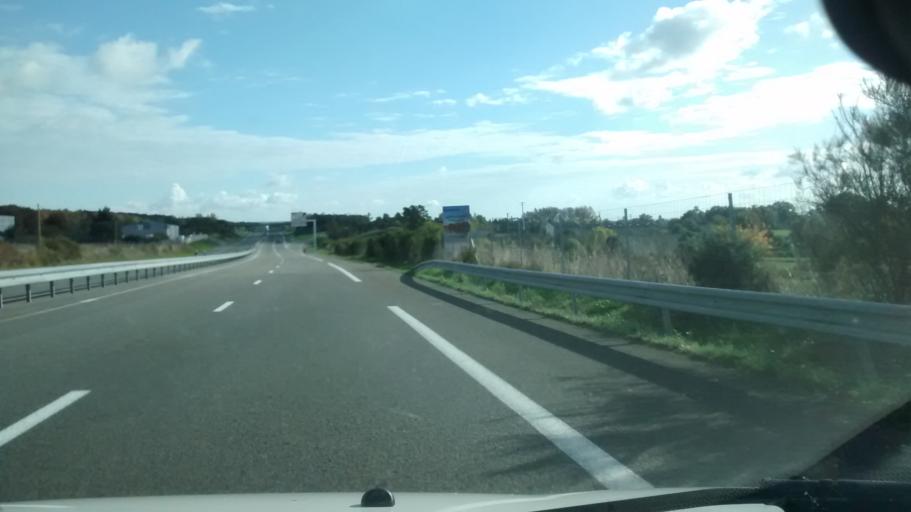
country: FR
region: Pays de la Loire
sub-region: Departement de Maine-et-Loire
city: Combree
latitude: 47.7196
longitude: -1.0344
